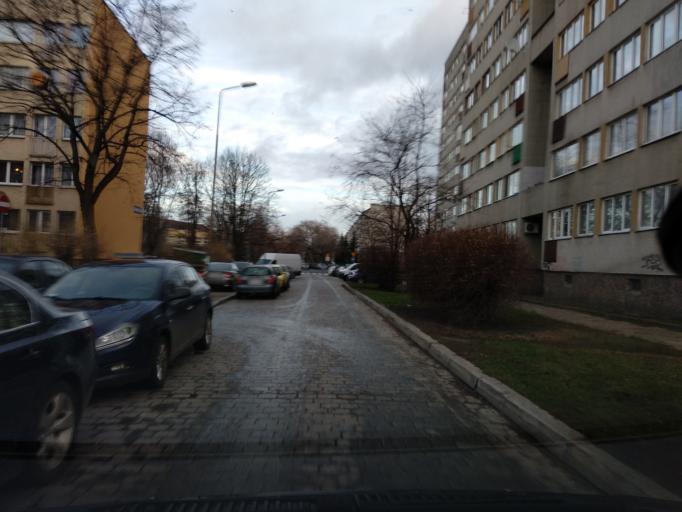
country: PL
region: Lower Silesian Voivodeship
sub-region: Powiat wroclawski
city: Wroclaw
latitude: 51.1165
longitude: 17.0029
